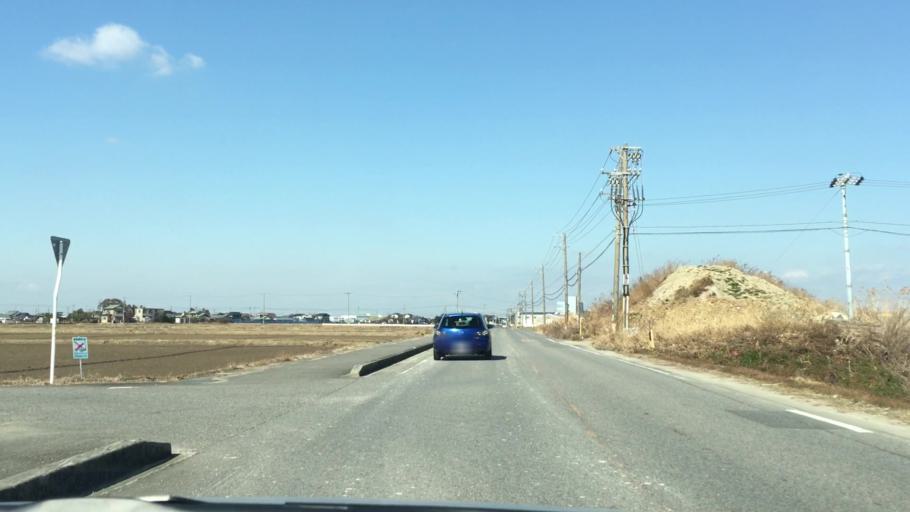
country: JP
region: Aichi
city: Anjo
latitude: 34.9822
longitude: 137.1183
